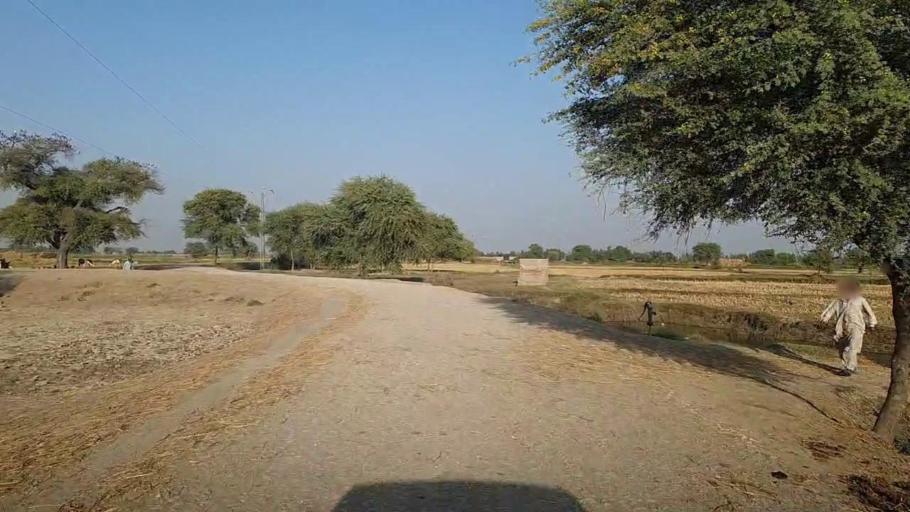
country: PK
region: Sindh
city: Kashmor
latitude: 28.4201
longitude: 69.4184
